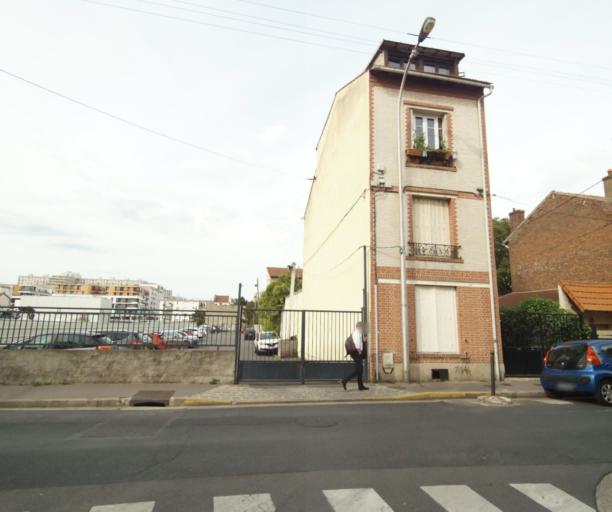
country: FR
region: Ile-de-France
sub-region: Departement des Hauts-de-Seine
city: Bois-Colombes
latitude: 48.9237
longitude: 2.2727
